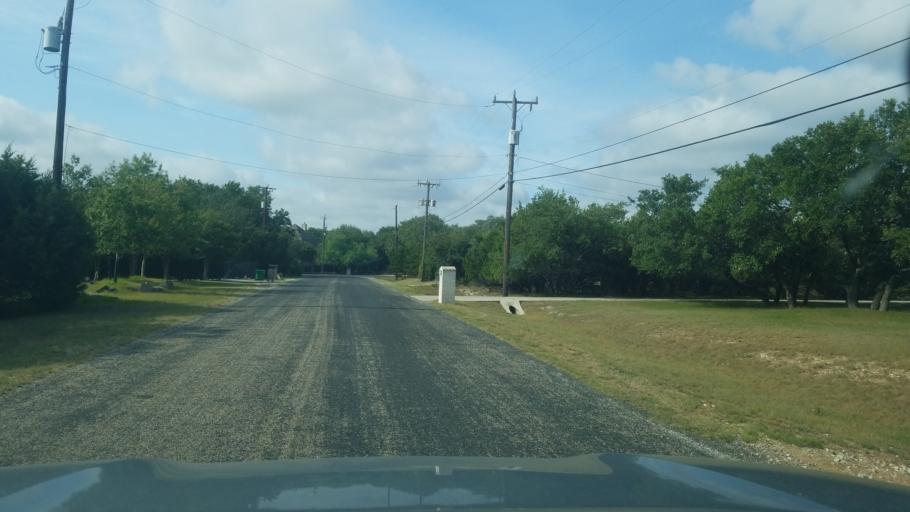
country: US
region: Texas
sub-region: Bexar County
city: Timberwood Park
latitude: 29.6970
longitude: -98.4998
